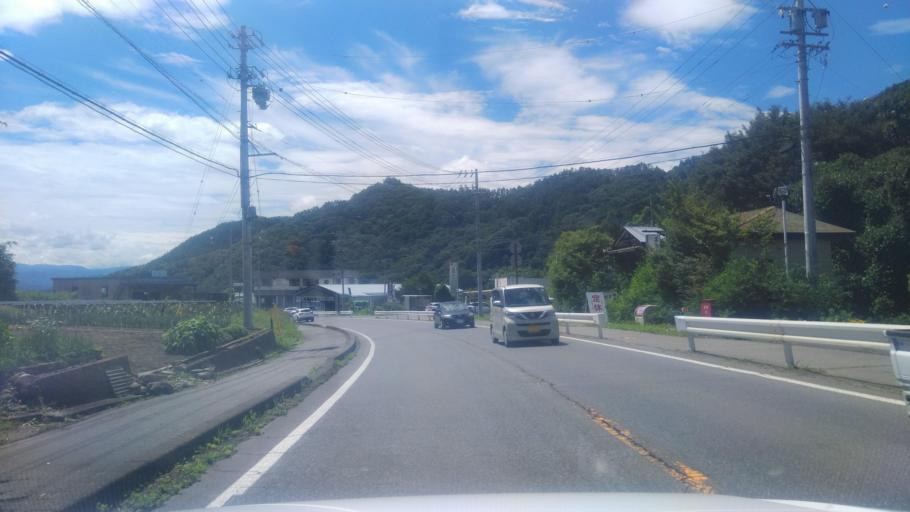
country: JP
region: Nagano
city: Ueda
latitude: 36.4356
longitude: 138.2996
